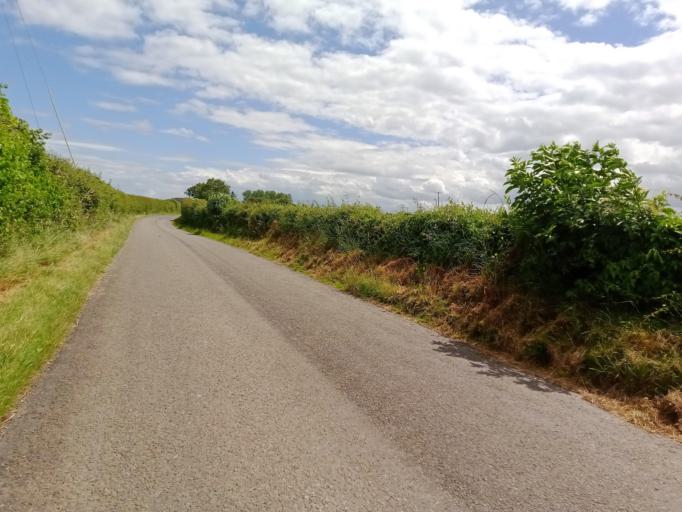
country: IE
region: Leinster
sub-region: Kilkenny
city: Kilkenny
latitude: 52.6795
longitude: -7.2434
